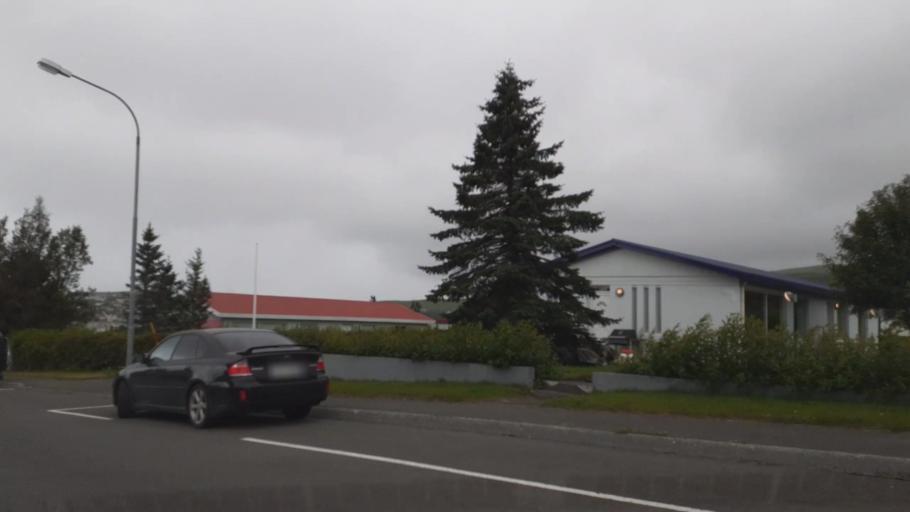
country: IS
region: Northeast
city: Husavik
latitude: 66.0395
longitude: -17.3359
